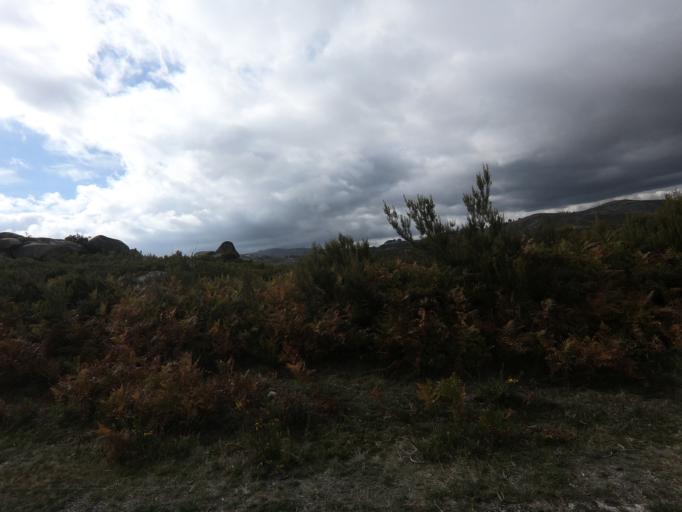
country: PT
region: Vila Real
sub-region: Vila Real
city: Vila Real
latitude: 41.3595
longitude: -7.7964
